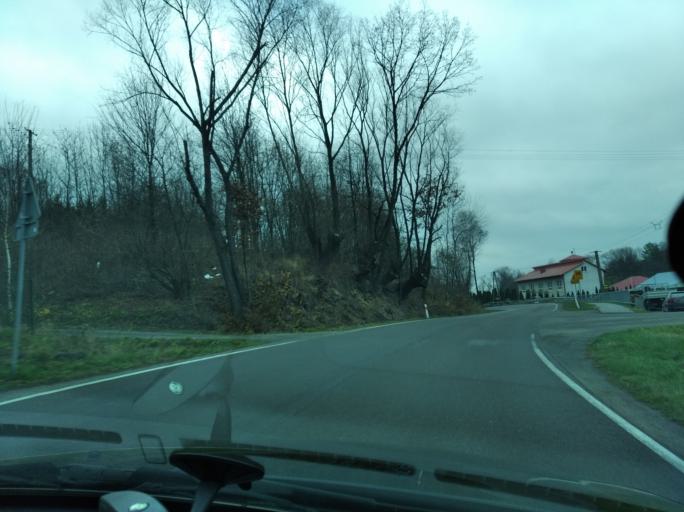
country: PL
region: Subcarpathian Voivodeship
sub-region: Powiat przeworski
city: Manasterz
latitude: 49.9273
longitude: 22.3365
